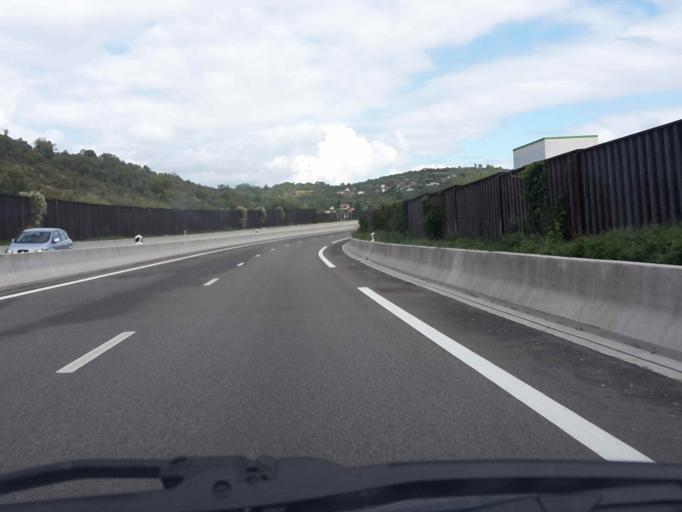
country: FR
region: Franche-Comte
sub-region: Departement du Doubs
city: Beure
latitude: 47.2125
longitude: 6.0001
